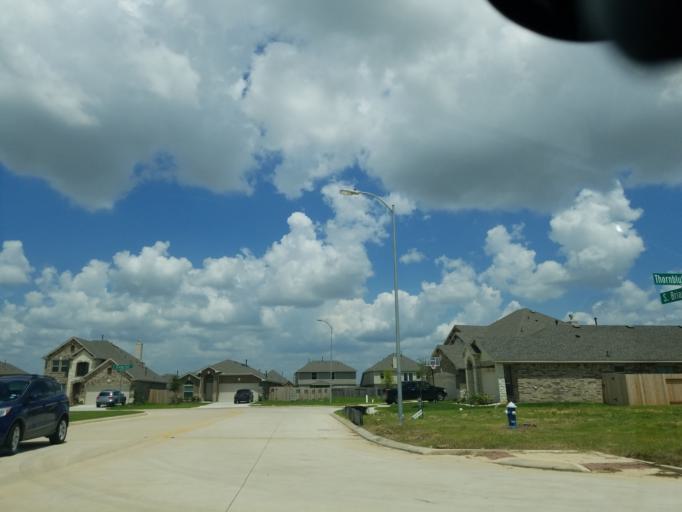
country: US
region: Texas
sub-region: Harris County
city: Katy
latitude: 29.8284
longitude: -95.7787
